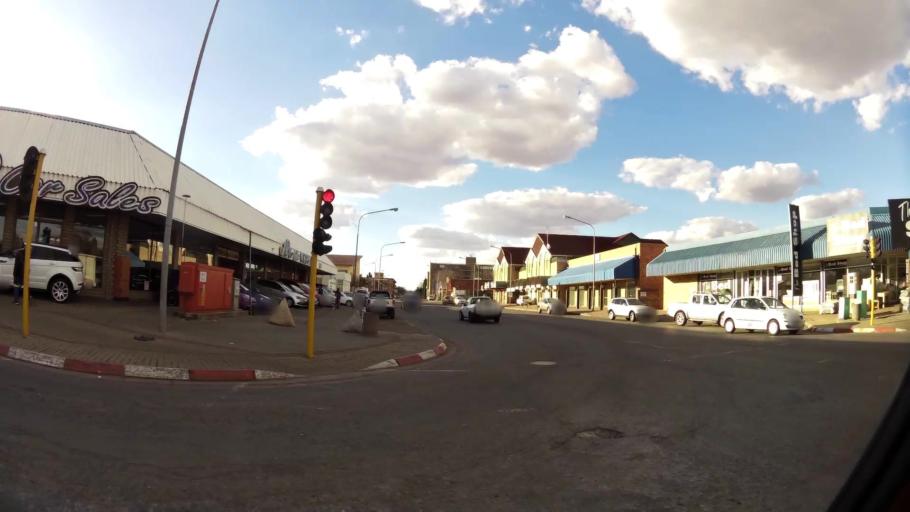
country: ZA
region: North-West
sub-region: Dr Kenneth Kaunda District Municipality
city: Potchefstroom
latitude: -26.7144
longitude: 27.0951
